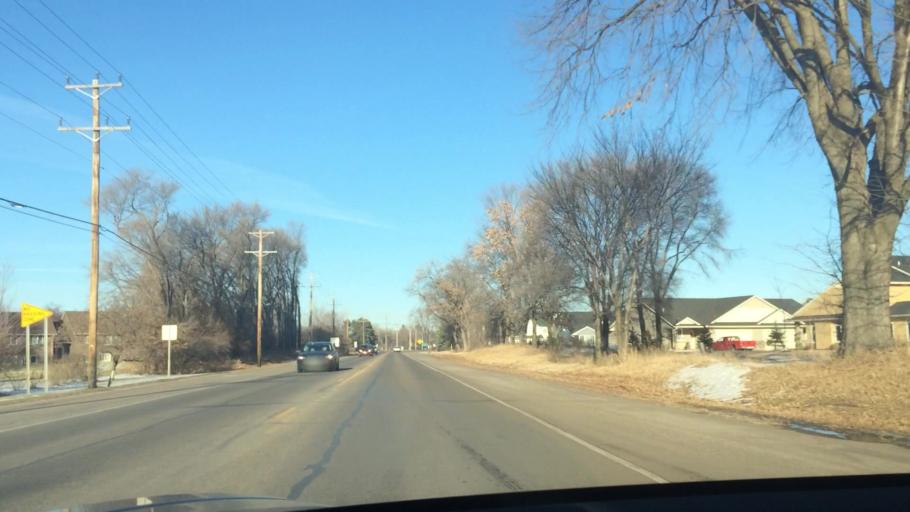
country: US
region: Minnesota
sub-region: Anoka County
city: Circle Pines
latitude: 45.1644
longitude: -93.1229
